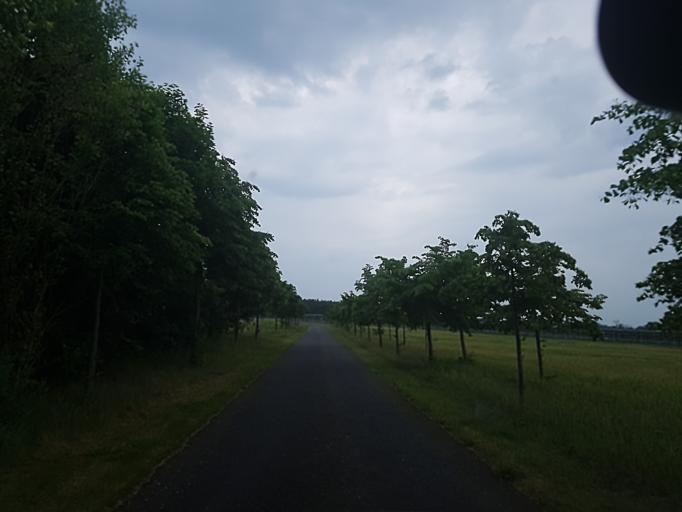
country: DE
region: Saxony-Anhalt
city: Elster
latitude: 51.8193
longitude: 12.8620
